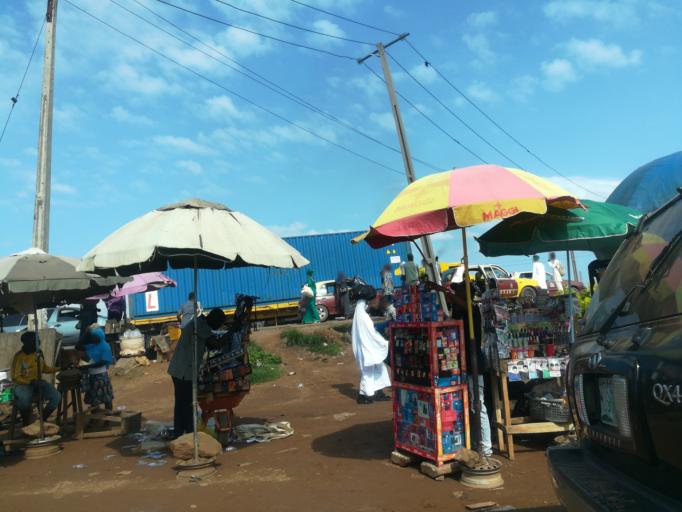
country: NG
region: Oyo
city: Ibadan
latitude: 7.4020
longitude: 3.9427
